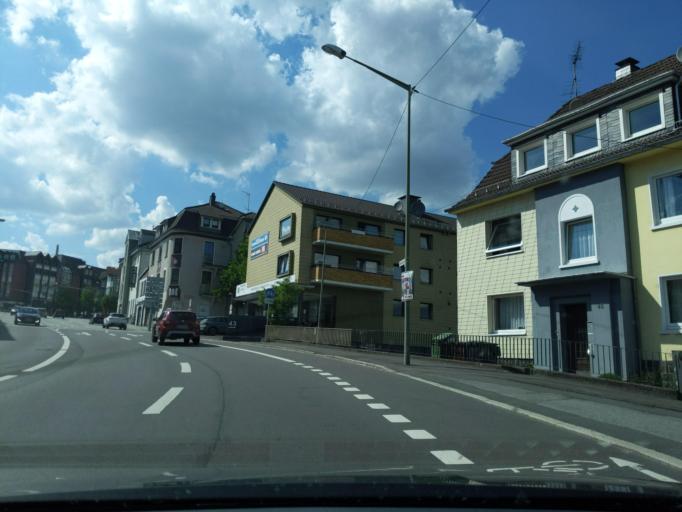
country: DE
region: North Rhine-Westphalia
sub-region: Regierungsbezirk Koln
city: Gummersbach
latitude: 51.0243
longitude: 7.5703
